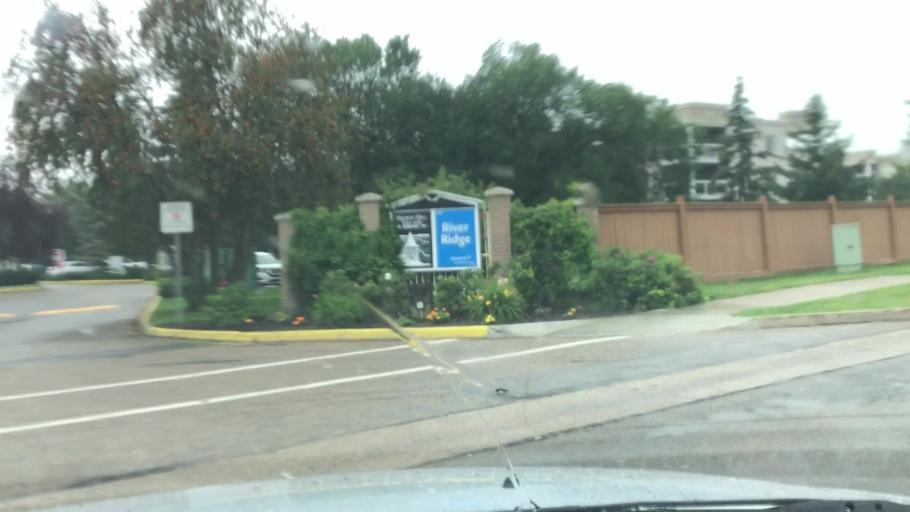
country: CA
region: Alberta
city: St. Albert
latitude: 53.6409
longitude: -113.6350
